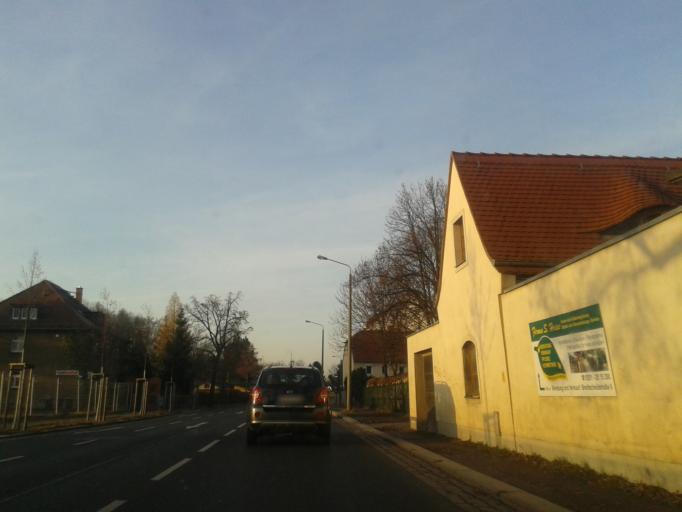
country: DE
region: Saxony
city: Heidenau
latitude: 51.0166
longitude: 13.8091
